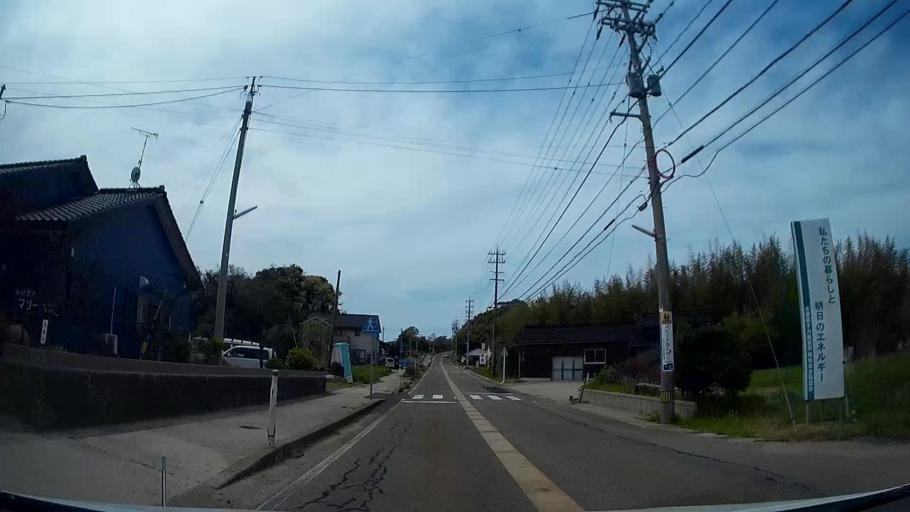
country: JP
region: Ishikawa
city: Hakui
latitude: 37.0071
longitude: 136.7681
